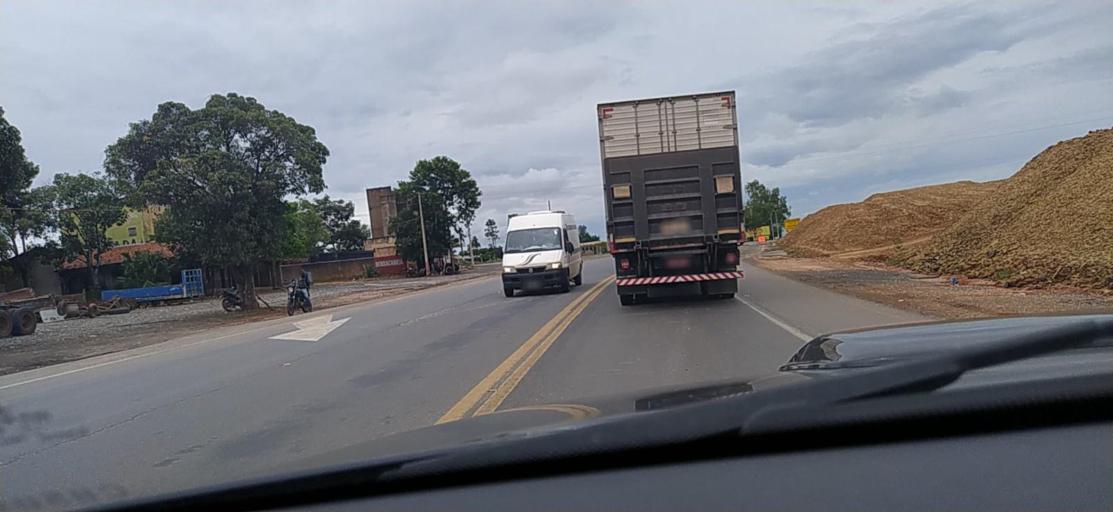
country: BR
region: Minas Gerais
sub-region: Curvelo
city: Curvelo
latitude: -18.7115
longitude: -44.4428
